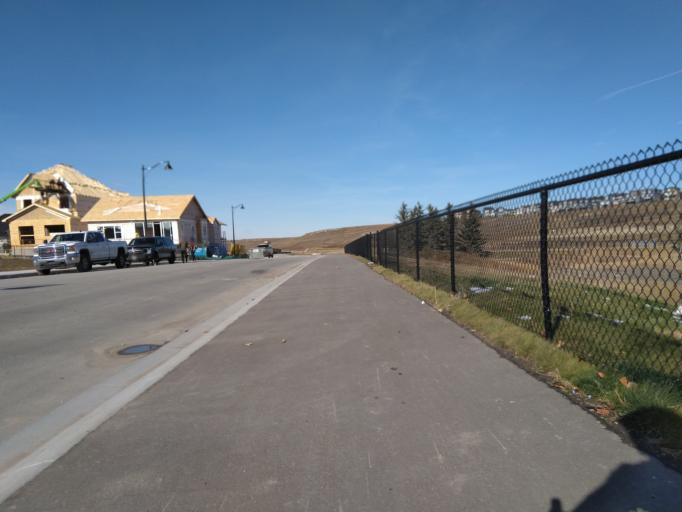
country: CA
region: Alberta
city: Calgary
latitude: 51.1767
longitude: -114.1297
